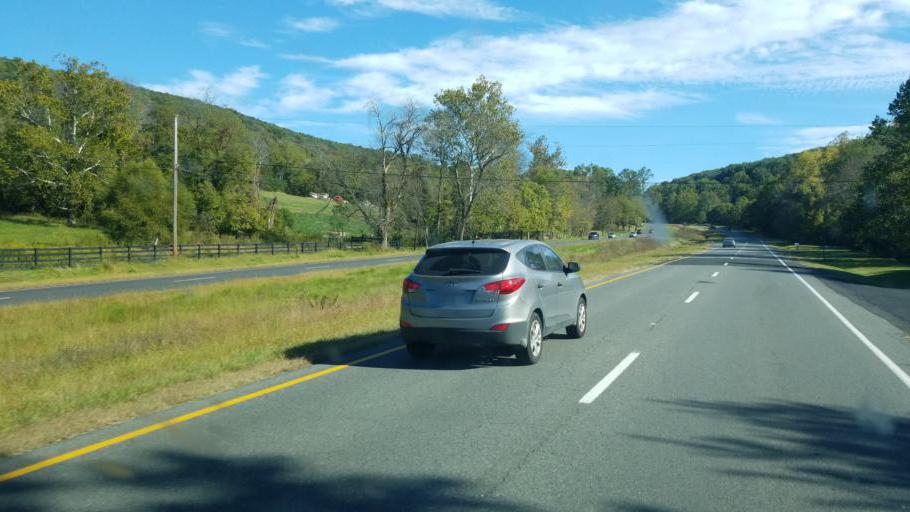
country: US
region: Virginia
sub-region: Warren County
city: Shenandoah Farms
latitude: 39.0236
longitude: -77.9748
